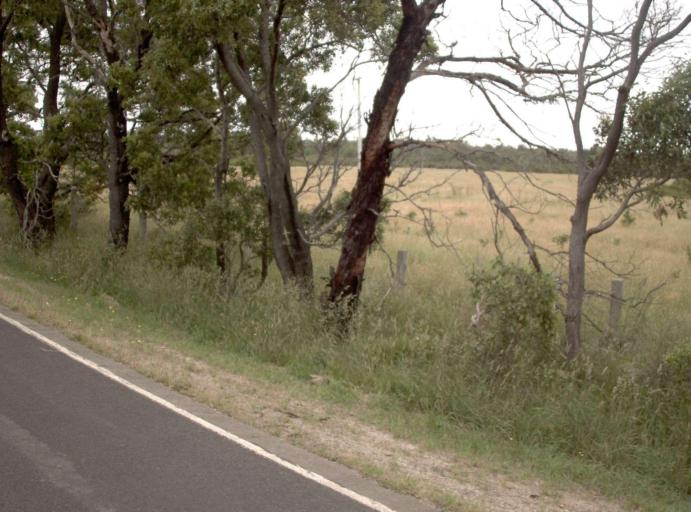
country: AU
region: Victoria
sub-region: Latrobe
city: Traralgon
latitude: -38.4906
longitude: 146.8193
